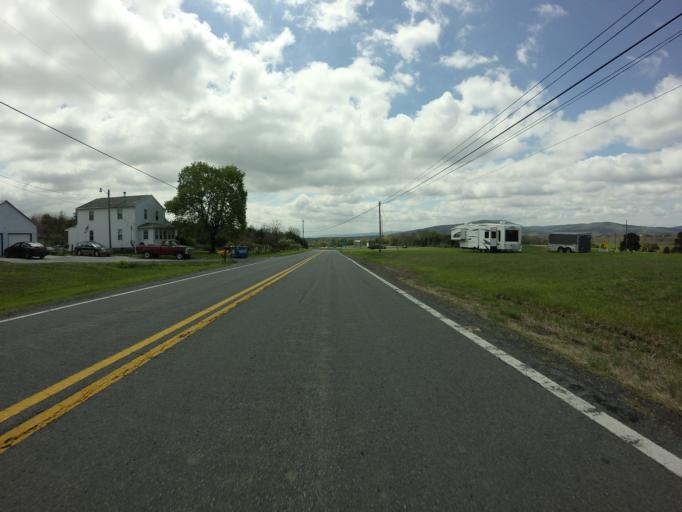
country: US
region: Maryland
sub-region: Frederick County
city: Emmitsburg
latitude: 39.7157
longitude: -77.3083
